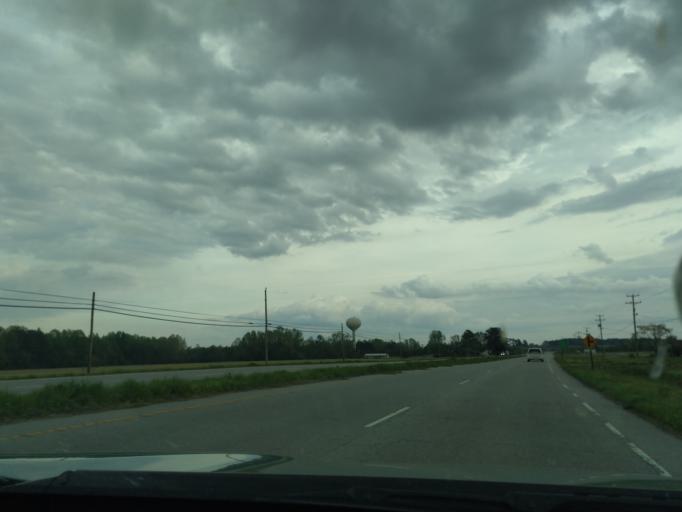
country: US
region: North Carolina
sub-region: Martin County
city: Williamston
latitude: 35.8258
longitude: -77.0657
